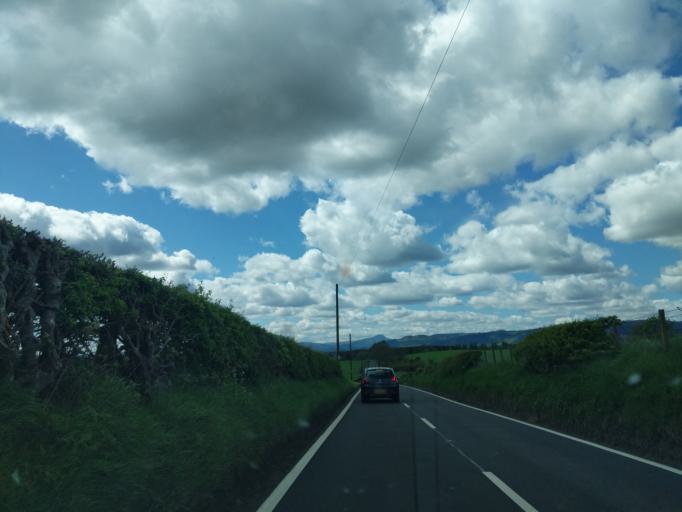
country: GB
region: Scotland
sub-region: Stirling
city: Doune
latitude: 56.1715
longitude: -4.1252
